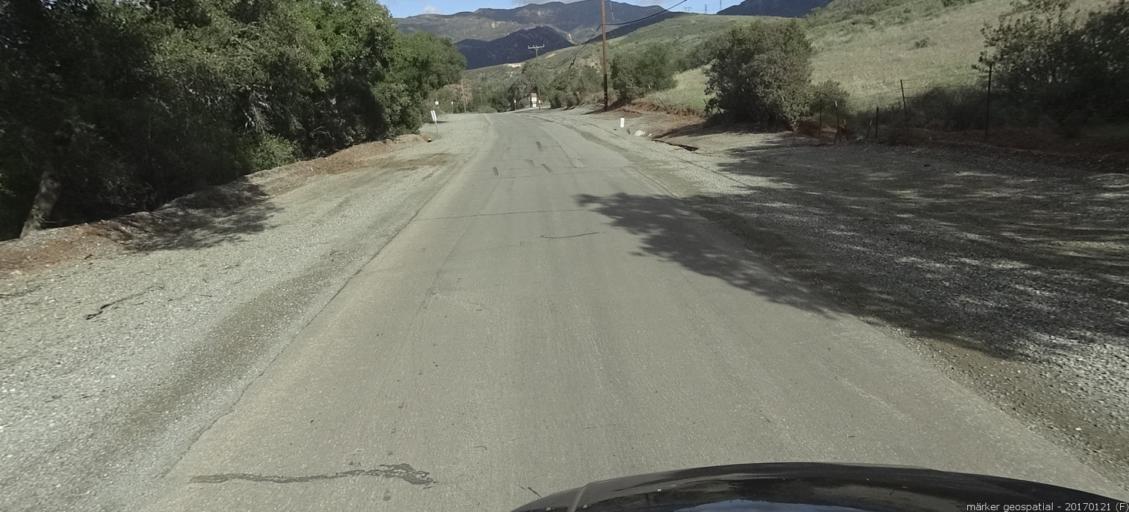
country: US
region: California
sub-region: Orange County
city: Foothill Ranch
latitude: 33.7569
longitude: -117.6770
